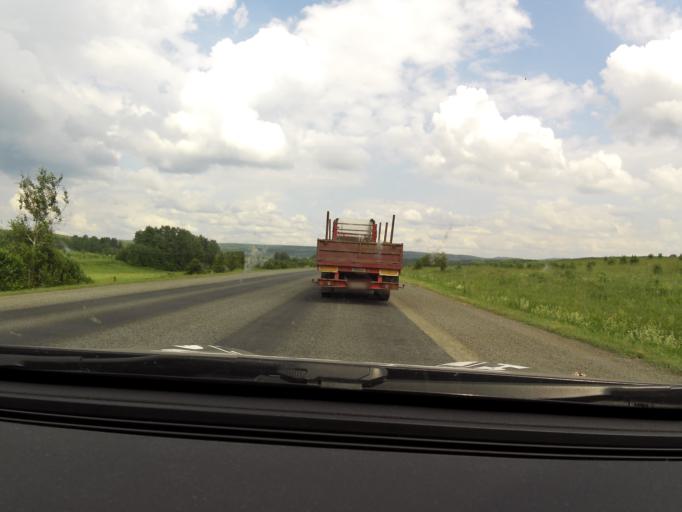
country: RU
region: Sverdlovsk
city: Ufimskiy
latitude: 56.7891
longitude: 58.3329
